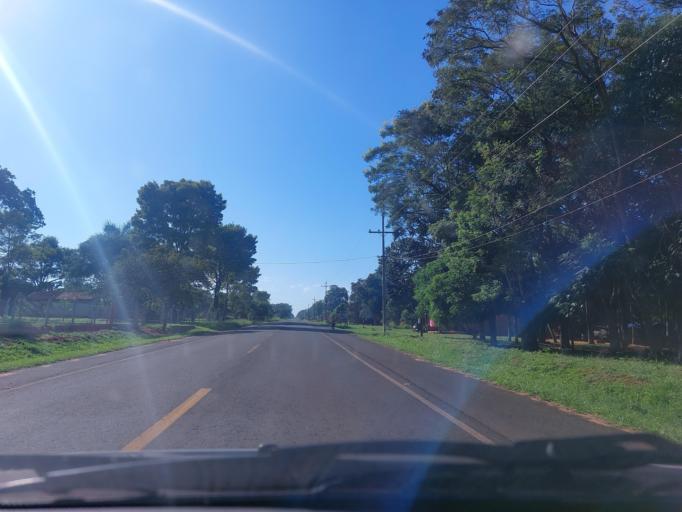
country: PY
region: San Pedro
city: Guayaybi
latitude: -24.5320
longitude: -56.4986
